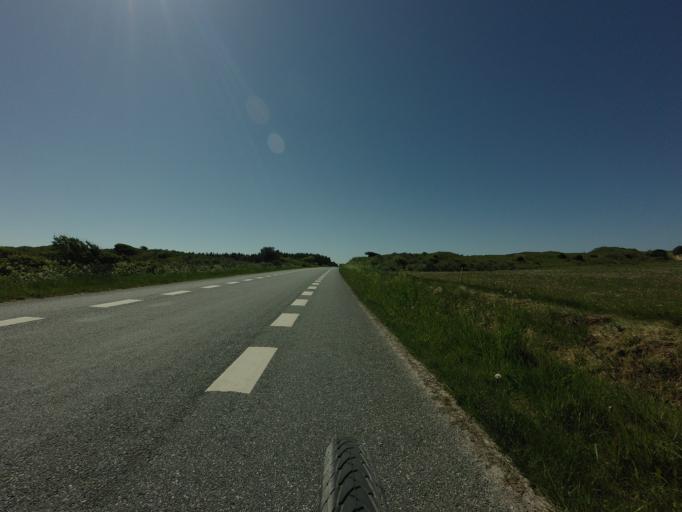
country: DK
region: North Denmark
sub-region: Hjorring Kommune
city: Hjorring
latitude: 57.4529
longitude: 9.7964
